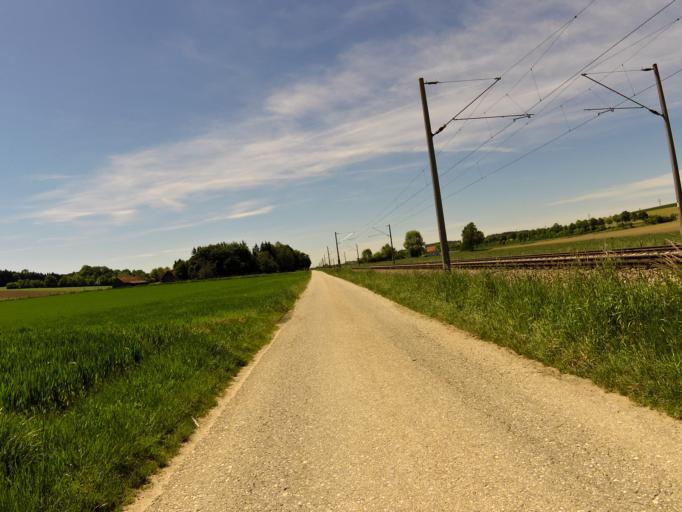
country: DE
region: Bavaria
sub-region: Upper Bavaria
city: Langenbach
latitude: 48.4309
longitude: 11.8421
